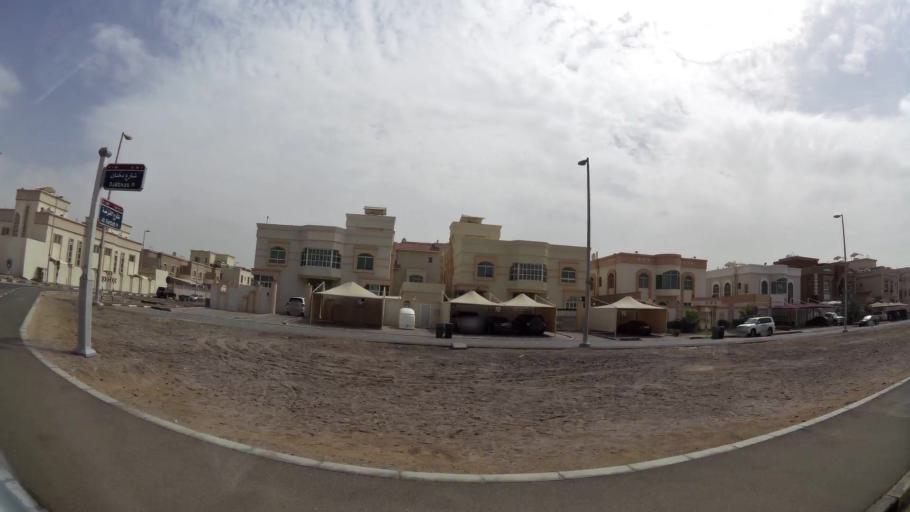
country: AE
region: Abu Dhabi
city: Abu Dhabi
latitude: 24.3963
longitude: 54.4932
